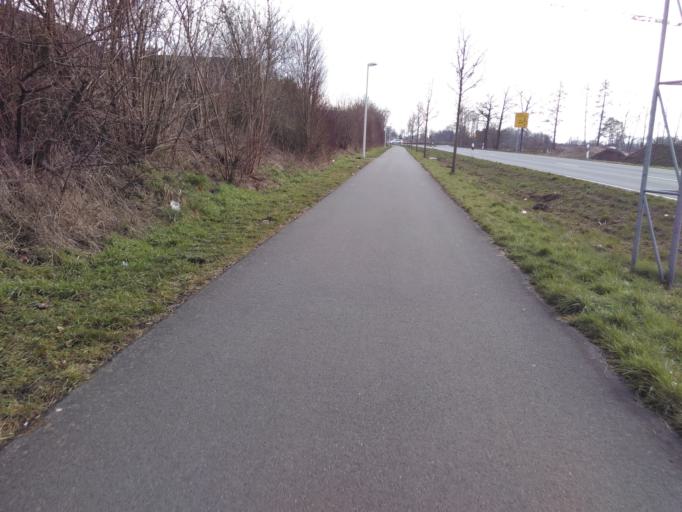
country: DE
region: North Rhine-Westphalia
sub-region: Regierungsbezirk Detmold
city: Verl
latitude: 51.8748
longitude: 8.4925
